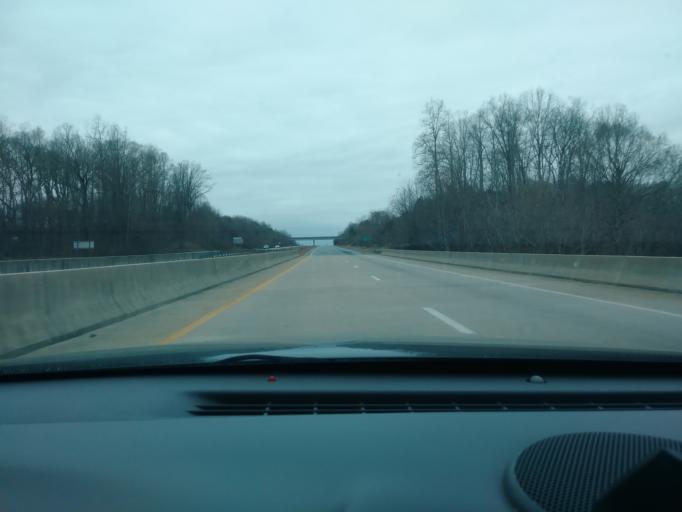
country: US
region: North Carolina
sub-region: Yadkin County
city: Yadkinville
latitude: 36.1185
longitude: -80.7228
